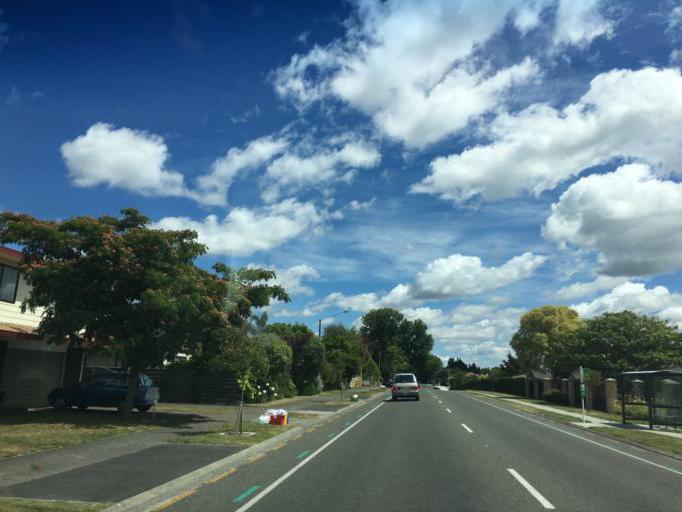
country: NZ
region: Hawke's Bay
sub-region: Hastings District
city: Hastings
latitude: -39.6510
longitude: 176.8664
